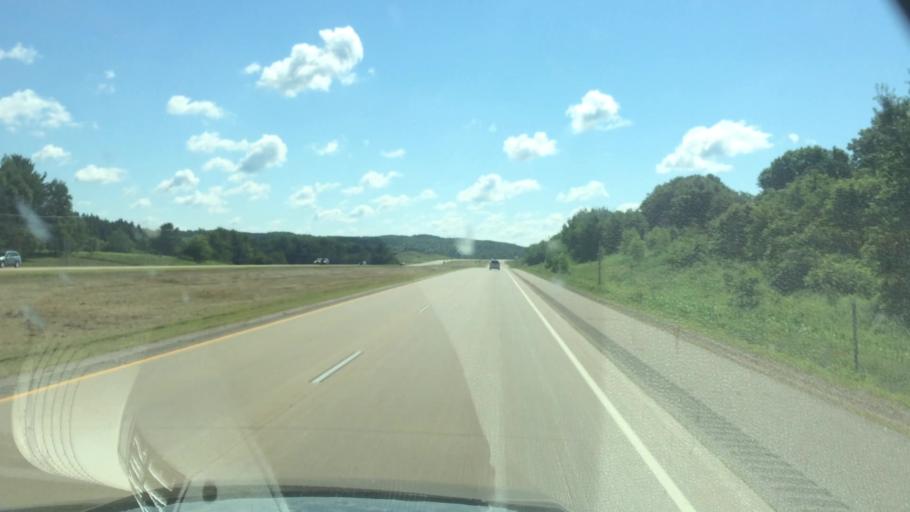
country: US
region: Wisconsin
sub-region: Portage County
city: Amherst
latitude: 44.5016
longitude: -89.3942
